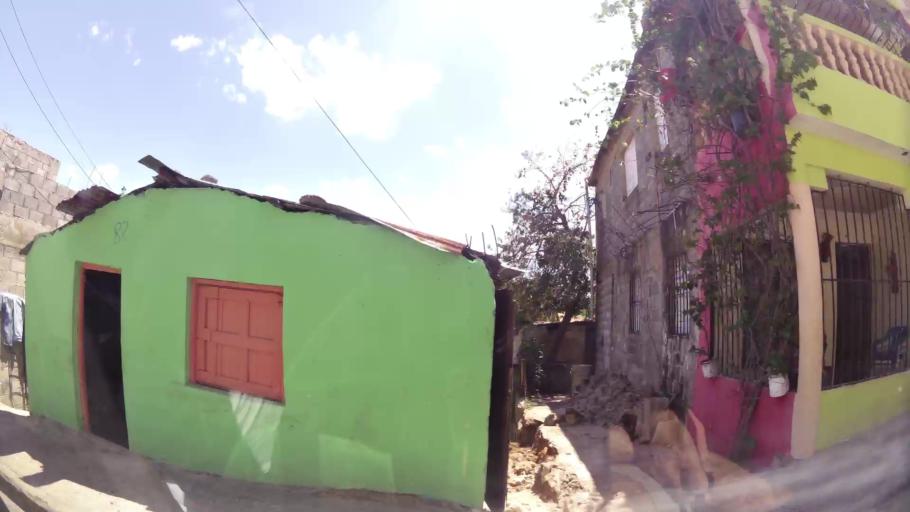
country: DO
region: San Cristobal
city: San Cristobal
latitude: 18.4020
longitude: -70.1109
